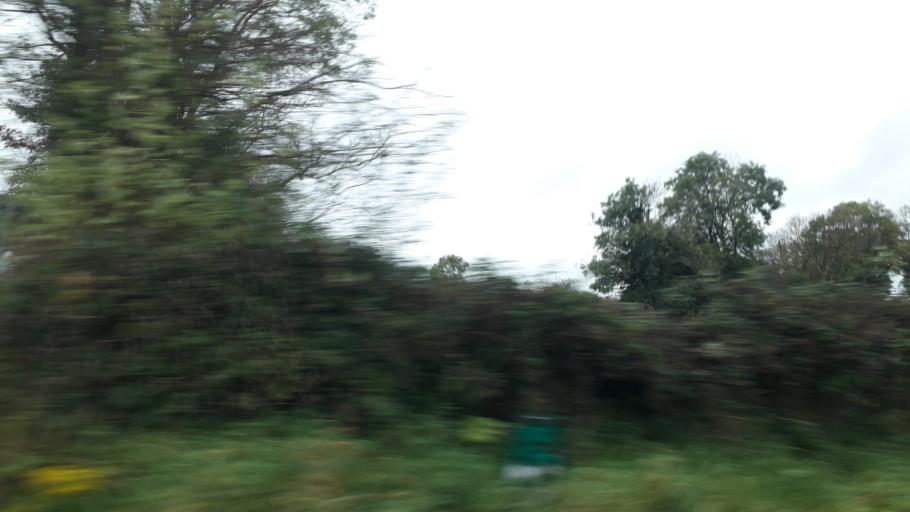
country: IE
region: Connaught
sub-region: Roscommon
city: Ballaghaderreen
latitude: 53.8935
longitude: -8.5566
